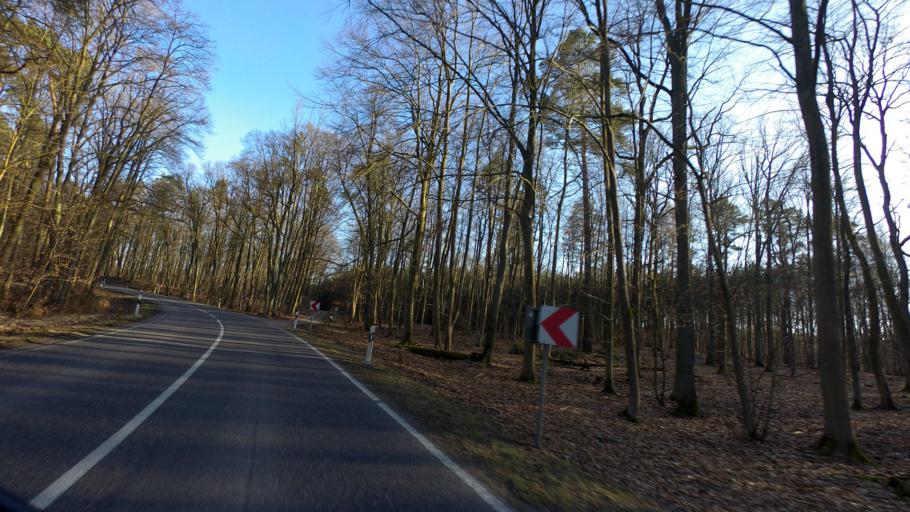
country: DE
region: Brandenburg
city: Joachimsthal
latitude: 52.9570
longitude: 13.7555
